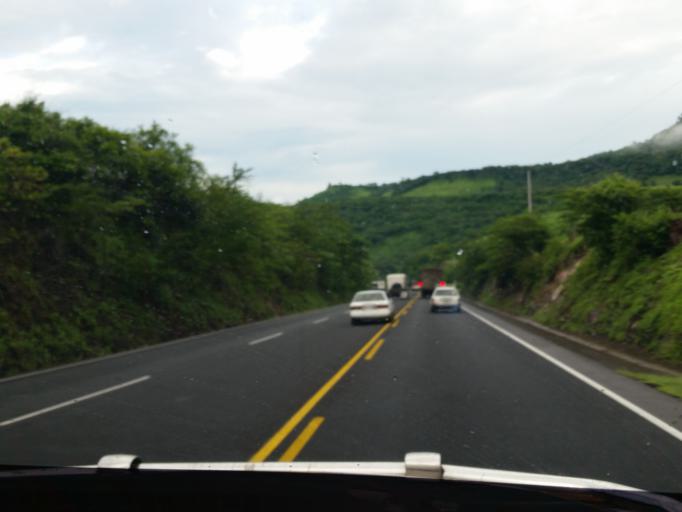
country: NI
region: Managua
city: Valle San Francisco
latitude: 12.4824
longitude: -86.0638
